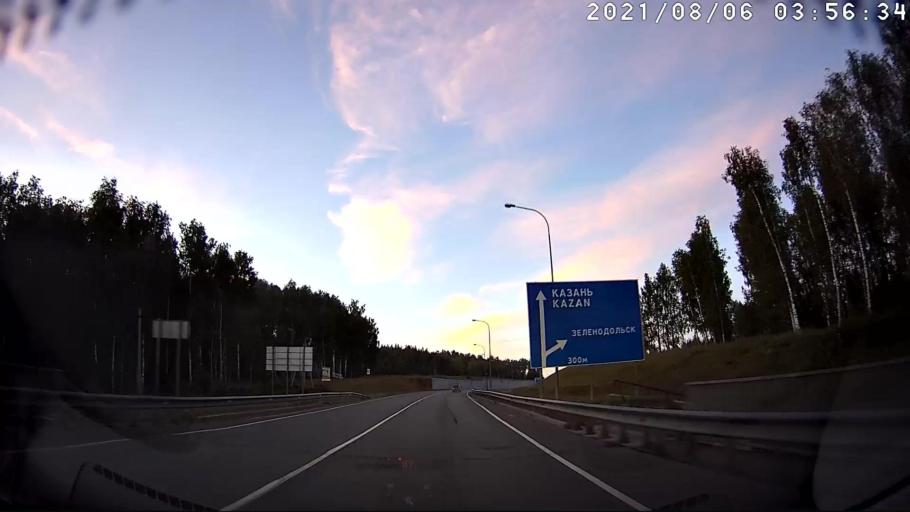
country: RU
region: Tatarstan
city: Aysha
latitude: 55.8774
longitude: 48.6575
